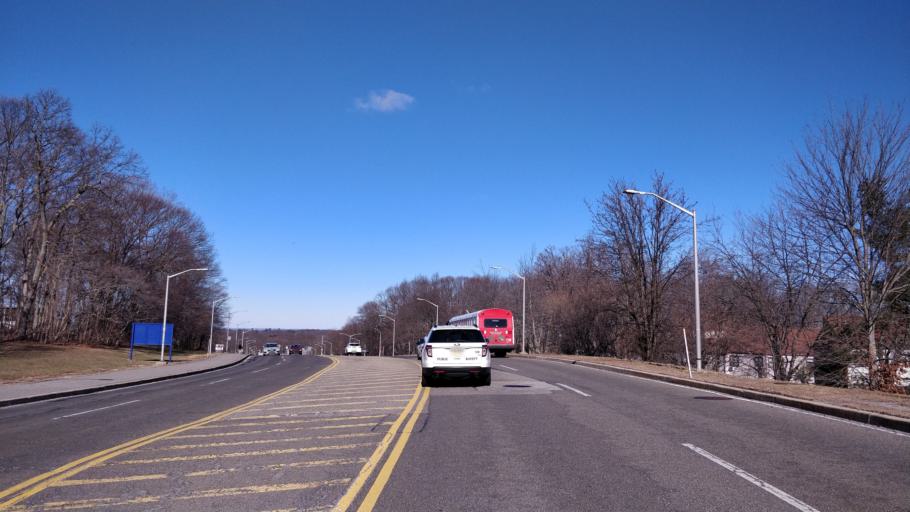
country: US
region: New York
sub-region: Suffolk County
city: Setauket-East Setauket
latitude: 40.9067
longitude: -73.1108
